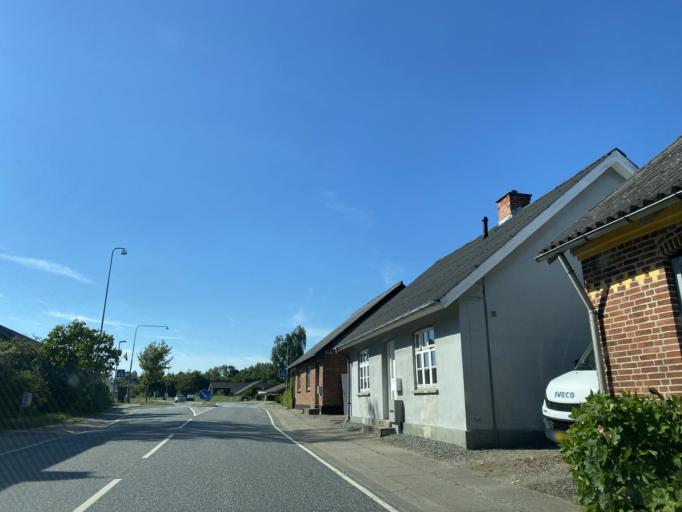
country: DK
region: Central Jutland
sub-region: Hedensted Kommune
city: Torring
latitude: 55.8618
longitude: 9.4147
